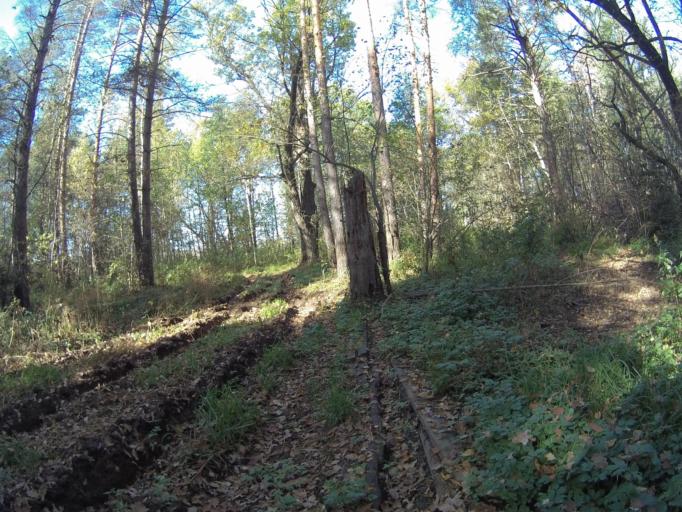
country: RU
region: Vladimir
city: Raduzhnyy
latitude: 56.0388
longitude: 40.3667
